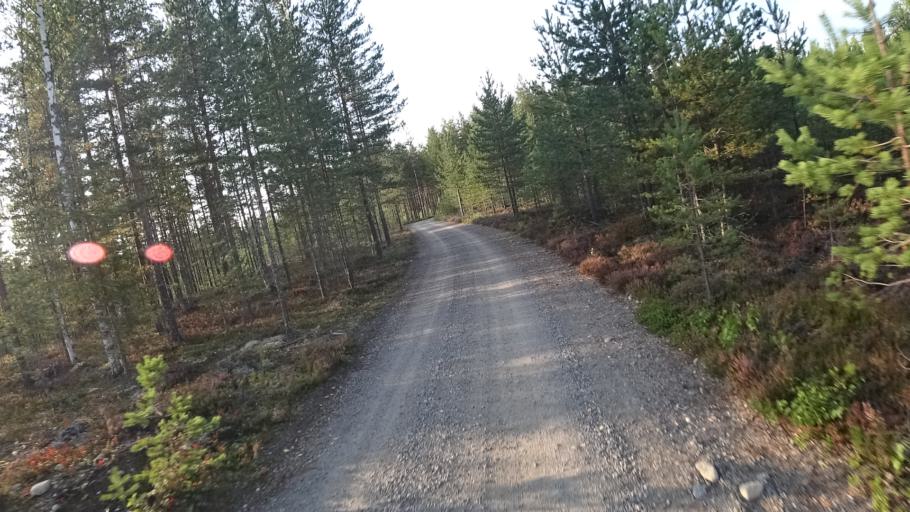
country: FI
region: North Karelia
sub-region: Joensuu
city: Ilomantsi
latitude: 62.6349
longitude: 31.0810
